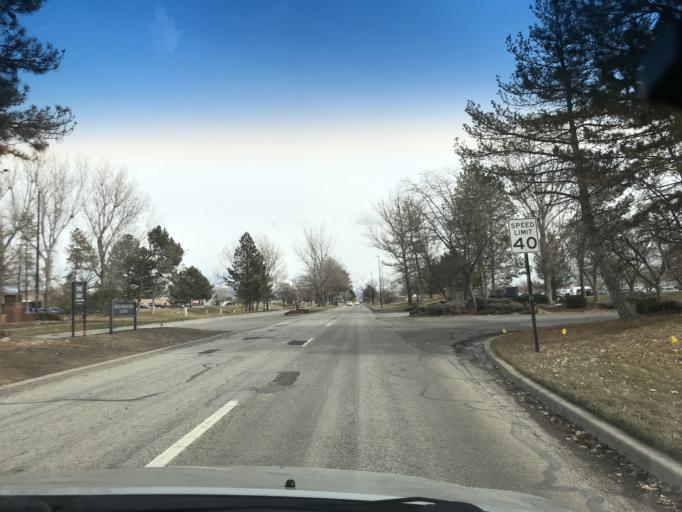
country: US
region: Utah
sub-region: Salt Lake County
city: West Valley City
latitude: 40.7763
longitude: -112.0125
